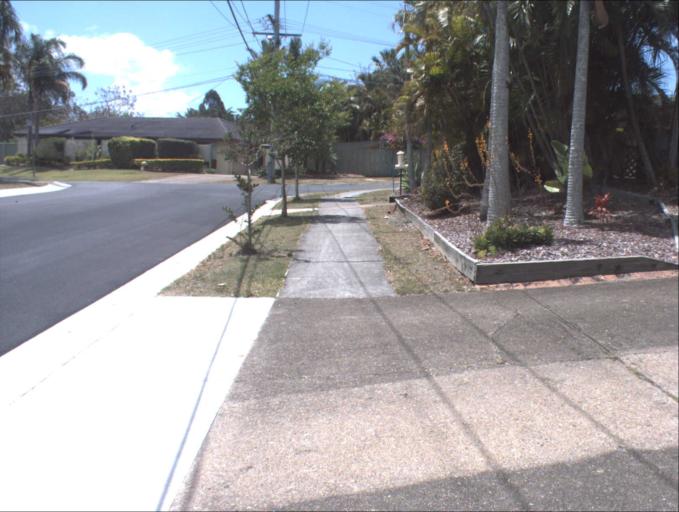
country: AU
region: Queensland
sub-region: Logan
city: Slacks Creek
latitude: -27.6547
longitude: 153.1753
